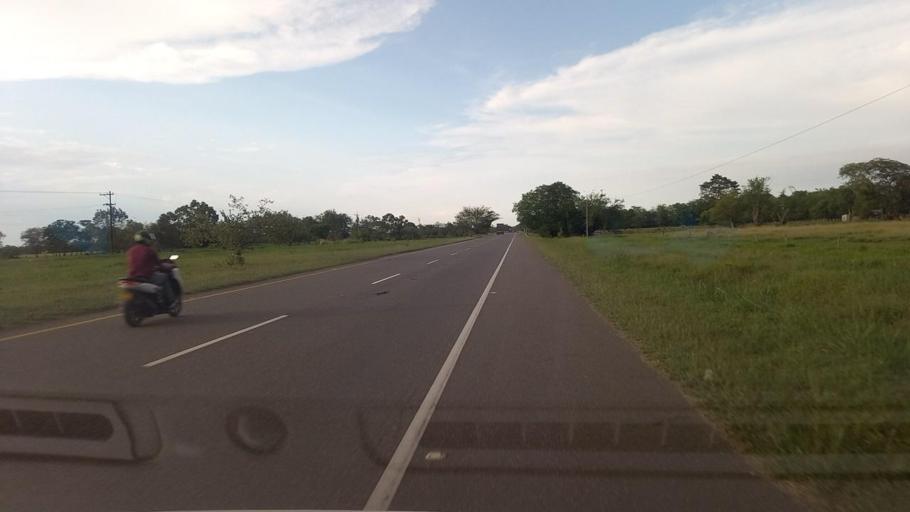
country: CO
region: Cundinamarca
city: Puerto Salgar
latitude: 5.5907
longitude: -74.6223
